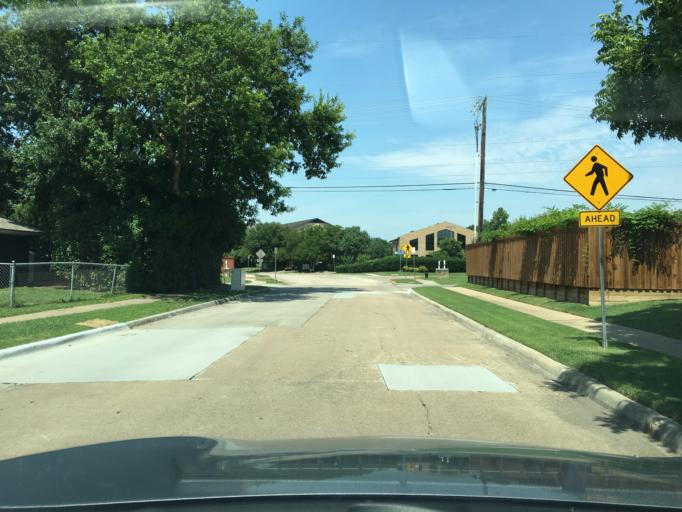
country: US
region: Texas
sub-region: Dallas County
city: Richardson
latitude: 32.9638
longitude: -96.6947
